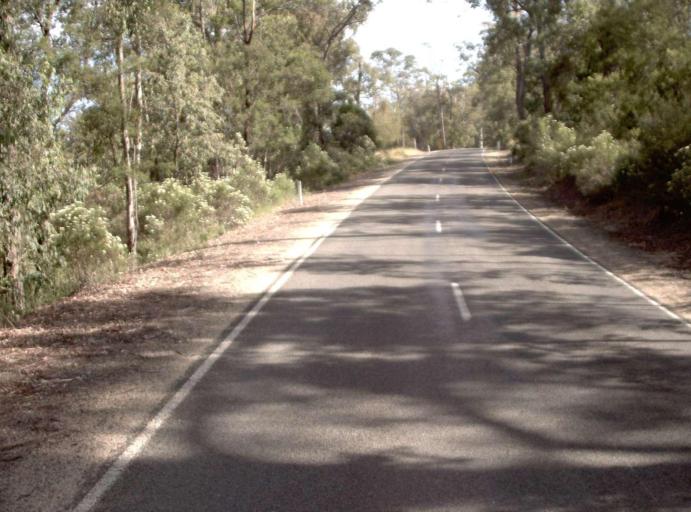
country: AU
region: Victoria
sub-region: East Gippsland
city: Lakes Entrance
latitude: -37.5458
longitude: 148.1478
